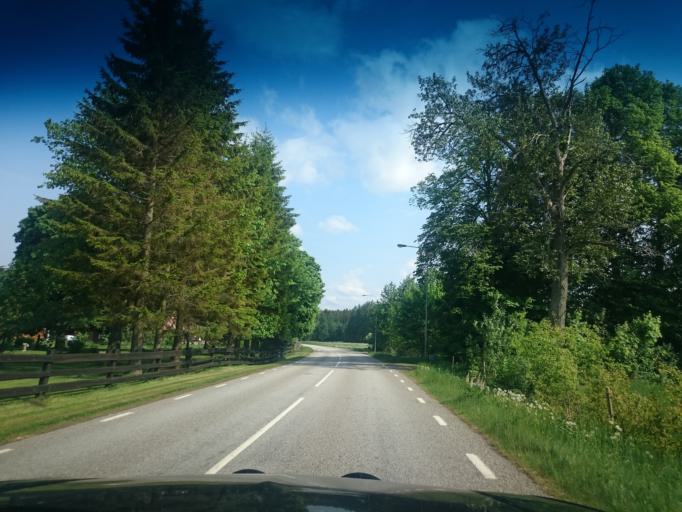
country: SE
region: Joenkoeping
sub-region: Vetlanda Kommun
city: Vetlanda
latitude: 57.3755
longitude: 15.0437
